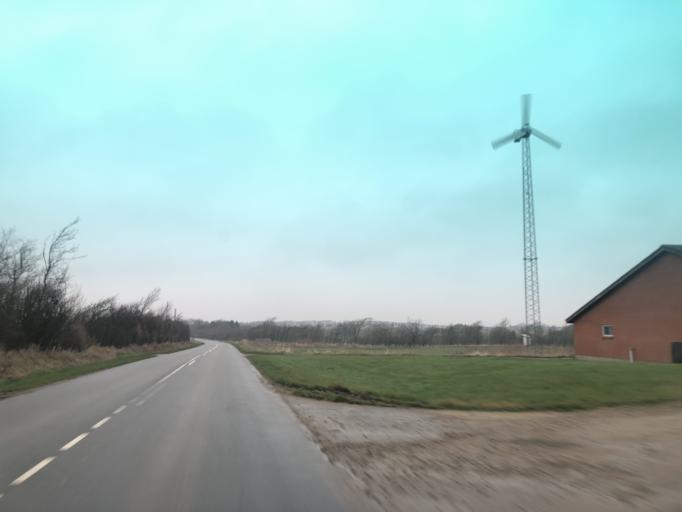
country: DK
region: North Denmark
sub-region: Thisted Kommune
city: Hurup
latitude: 56.7392
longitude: 8.4181
